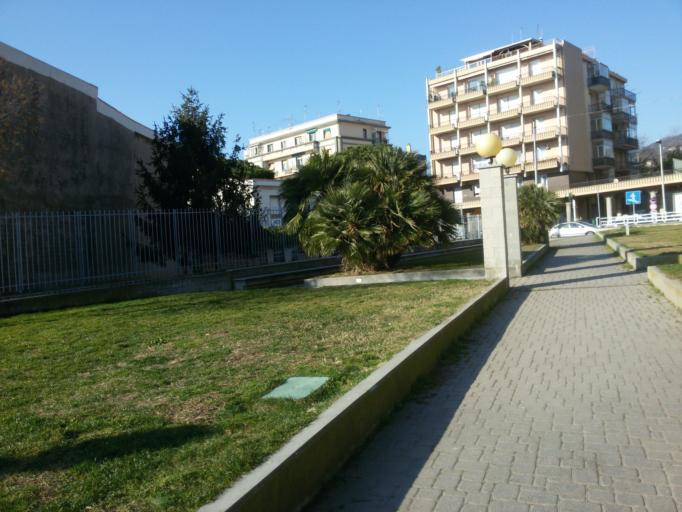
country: IT
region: Liguria
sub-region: Provincia di Savona
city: Savona
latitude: 44.2975
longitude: 8.4659
